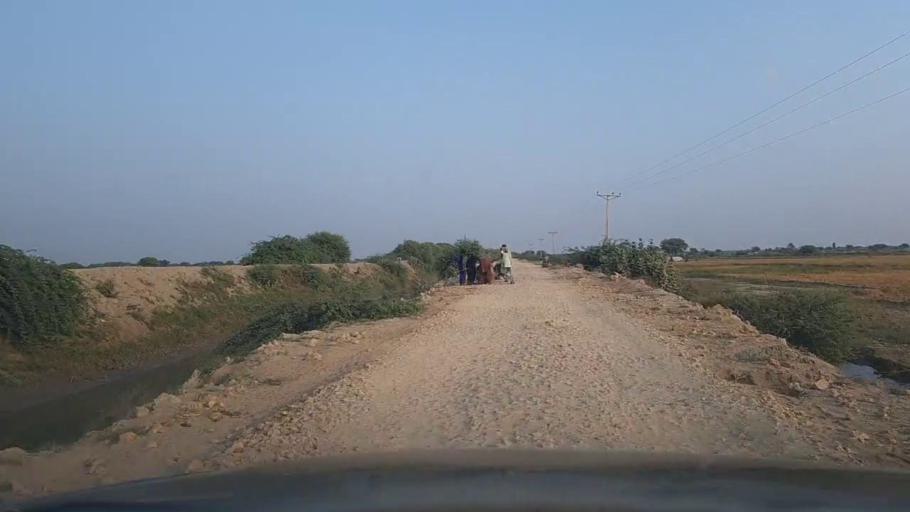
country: PK
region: Sindh
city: Mirpur Batoro
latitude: 24.5456
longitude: 68.3544
